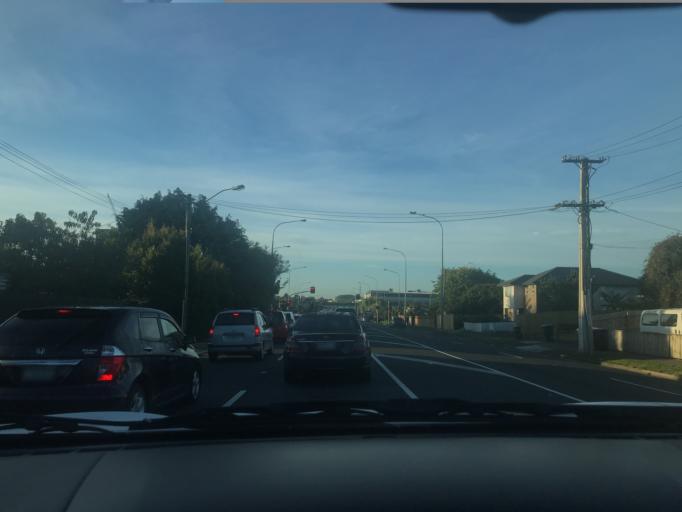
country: NZ
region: Auckland
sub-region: Auckland
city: Tamaki
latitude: -36.9122
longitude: 174.8383
